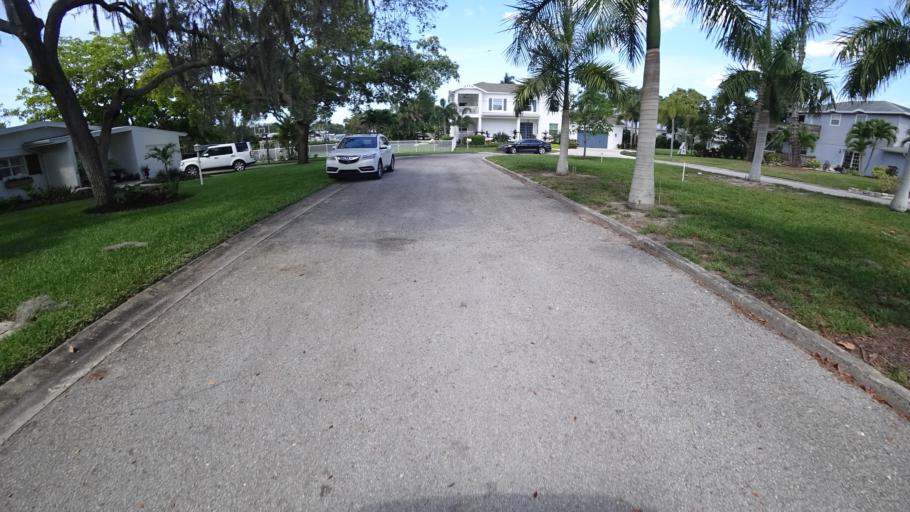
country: US
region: Florida
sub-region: Manatee County
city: West Bradenton
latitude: 27.5065
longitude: -82.6260
